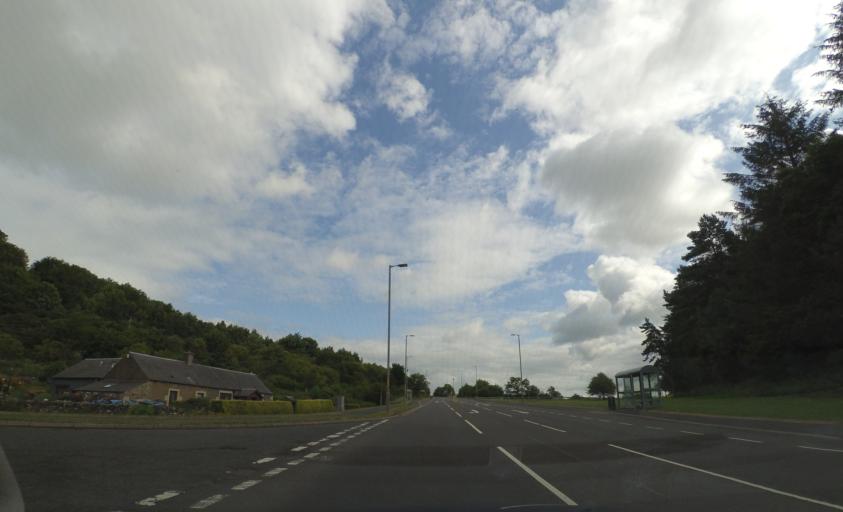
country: GB
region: Scotland
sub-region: The Scottish Borders
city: Hawick
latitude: 55.4373
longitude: -2.7789
